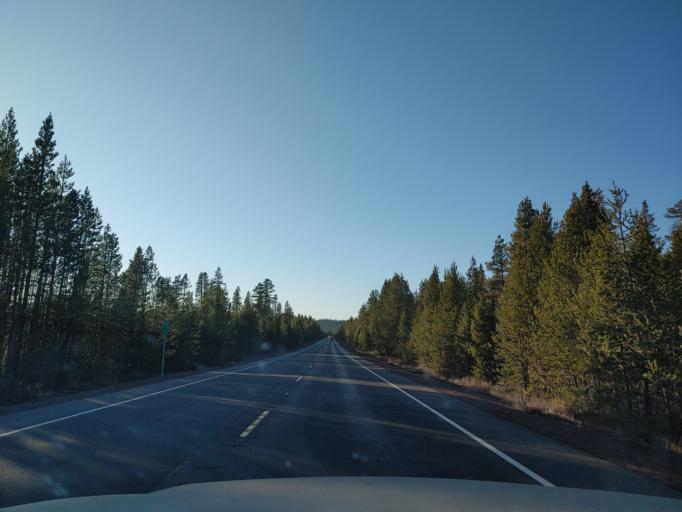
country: US
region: Oregon
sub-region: Deschutes County
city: La Pine
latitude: 43.4278
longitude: -121.8498
